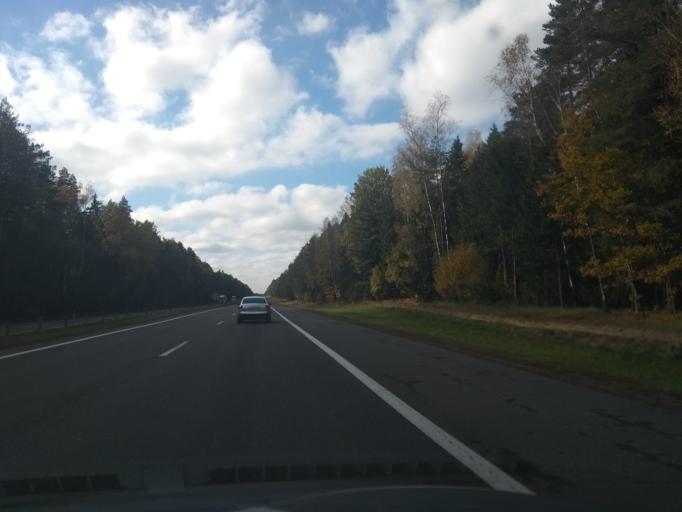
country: BY
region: Minsk
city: Enyerhyetykaw
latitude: 53.5676
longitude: 26.9949
